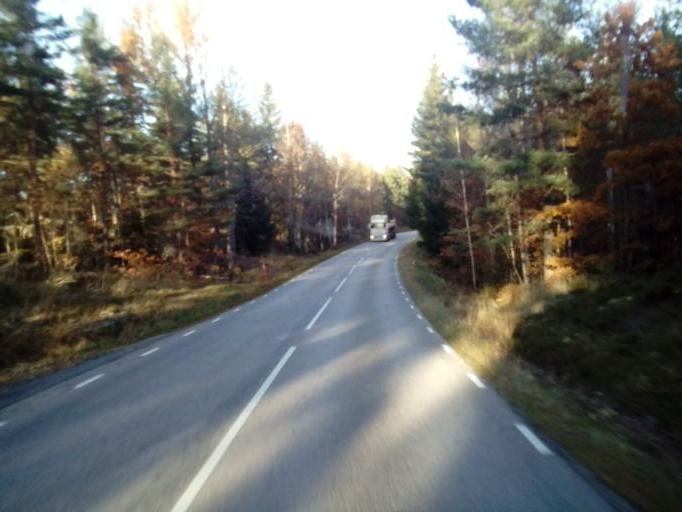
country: SE
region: Kalmar
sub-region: Vasterviks Kommun
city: Ankarsrum
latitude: 57.7683
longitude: 16.1385
